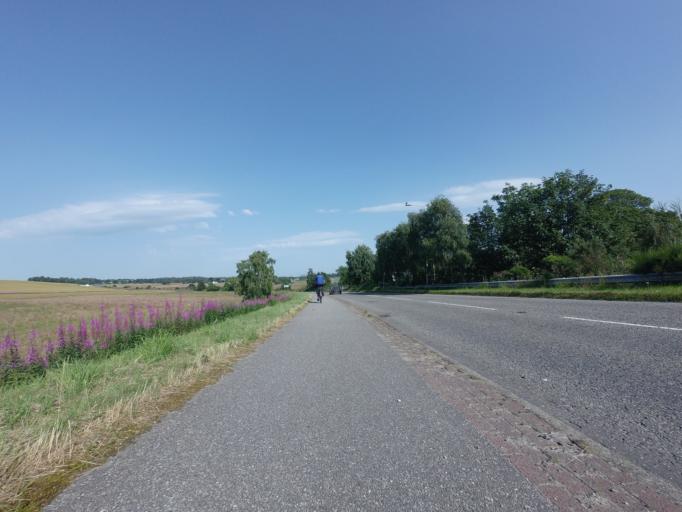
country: GB
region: Scotland
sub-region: Highland
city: Alness
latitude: 57.6836
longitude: -4.2944
